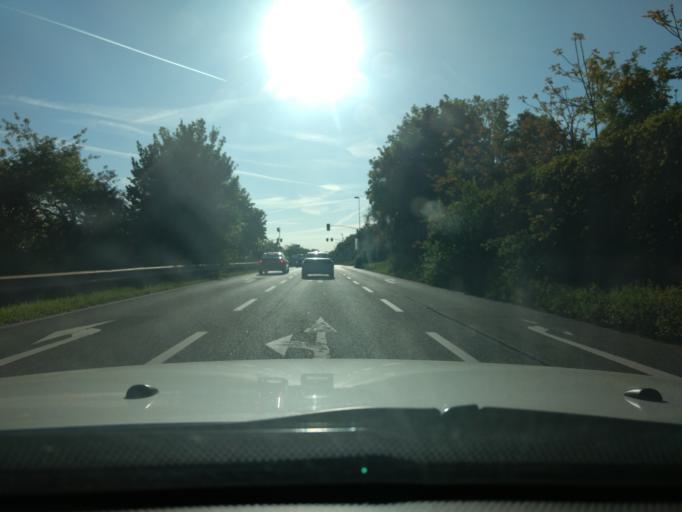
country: DE
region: North Rhine-Westphalia
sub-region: Regierungsbezirk Dusseldorf
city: Dusseldorf
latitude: 51.2406
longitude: 6.7422
